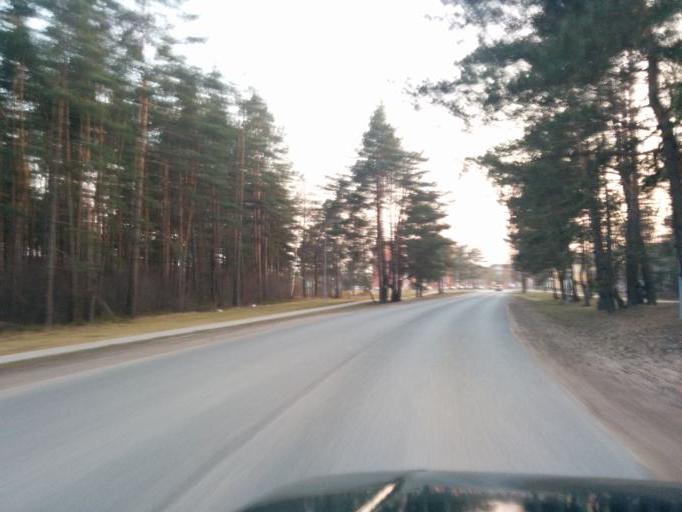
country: LV
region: Kekava
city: Balozi
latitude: 56.8779
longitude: 24.1255
